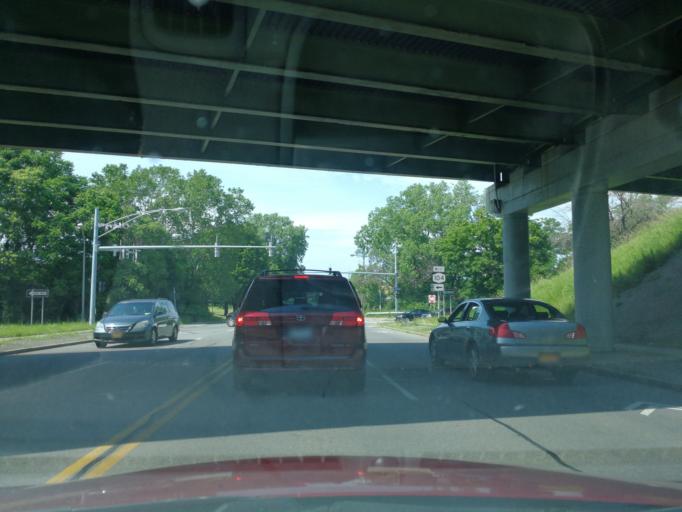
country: US
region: New York
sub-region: Monroe County
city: Irondequoit
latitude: 43.1934
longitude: -77.5922
